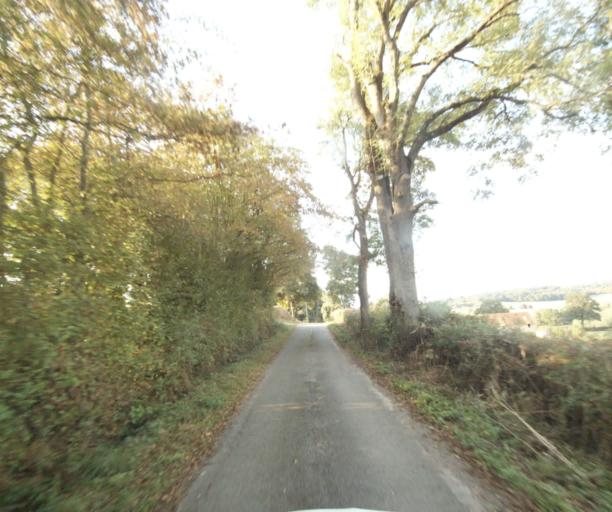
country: FR
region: Bourgogne
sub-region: Departement de Saone-et-Loire
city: Charolles
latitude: 46.4421
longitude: 4.3615
